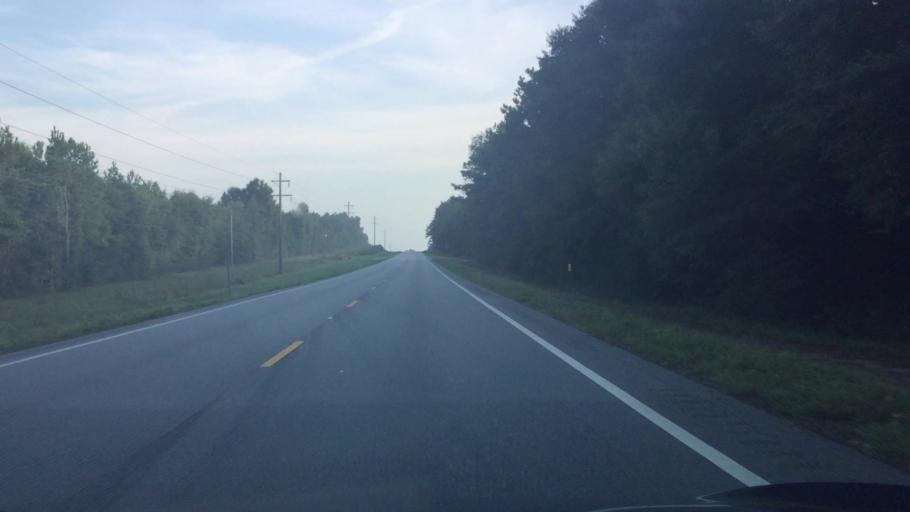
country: US
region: Alabama
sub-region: Covington County
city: Florala
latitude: 31.0658
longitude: -86.3995
